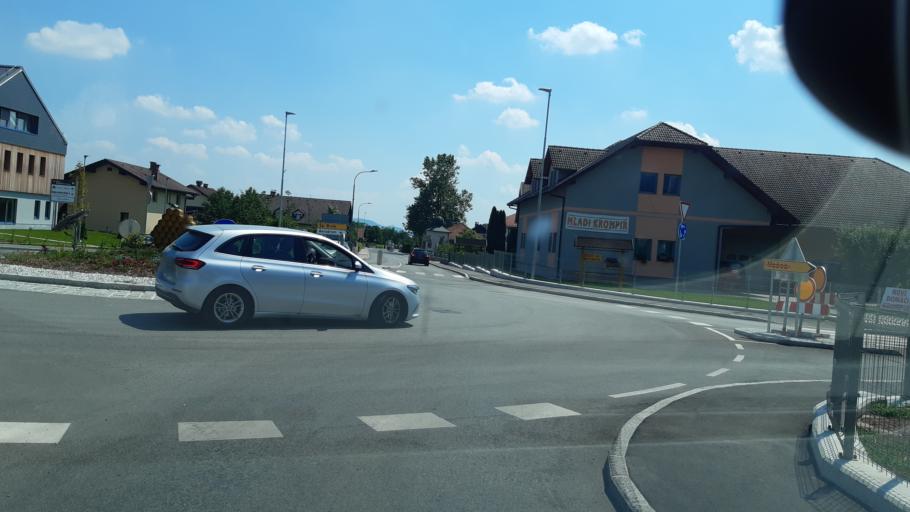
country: SI
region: Cerklje na Gorenjskem
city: Cerklje na Gorenjskem
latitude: 46.2503
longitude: 14.4861
